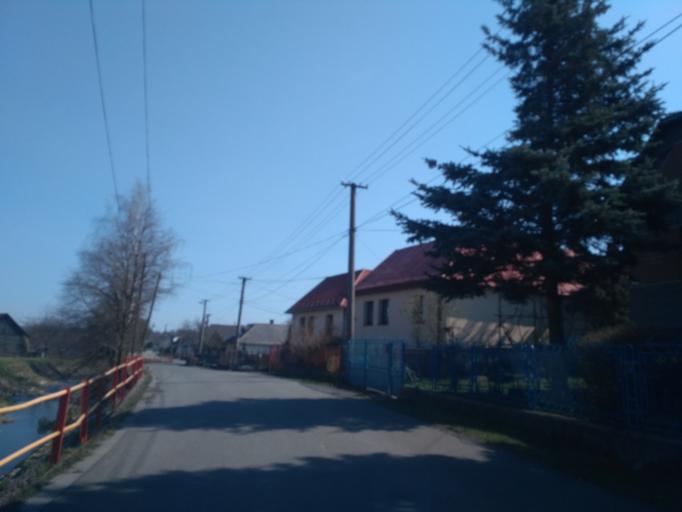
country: SK
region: Presovsky
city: Vranov nad Topl'ou
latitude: 48.8250
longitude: 21.6338
